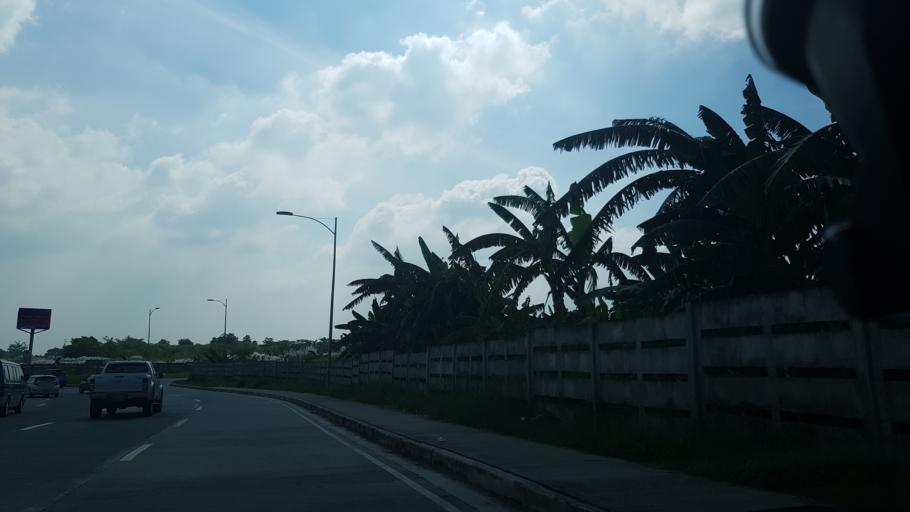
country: PH
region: Calabarzon
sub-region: Province of Laguna
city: San Pedro
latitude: 14.3731
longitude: 121.0131
